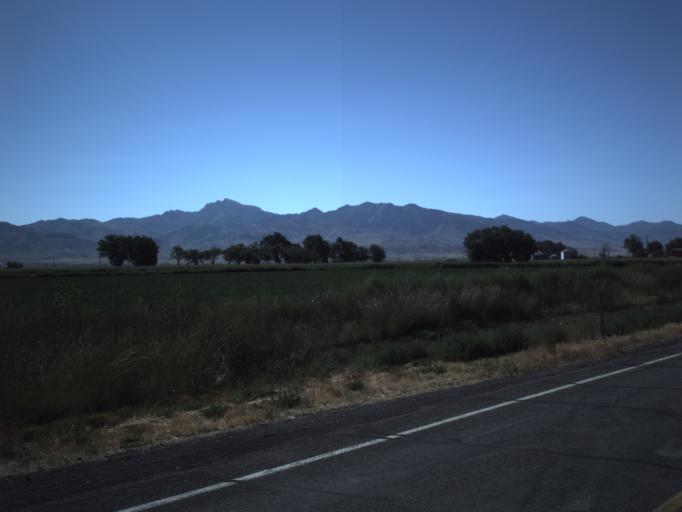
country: US
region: Utah
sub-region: Millard County
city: Delta
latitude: 39.5237
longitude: -112.3720
